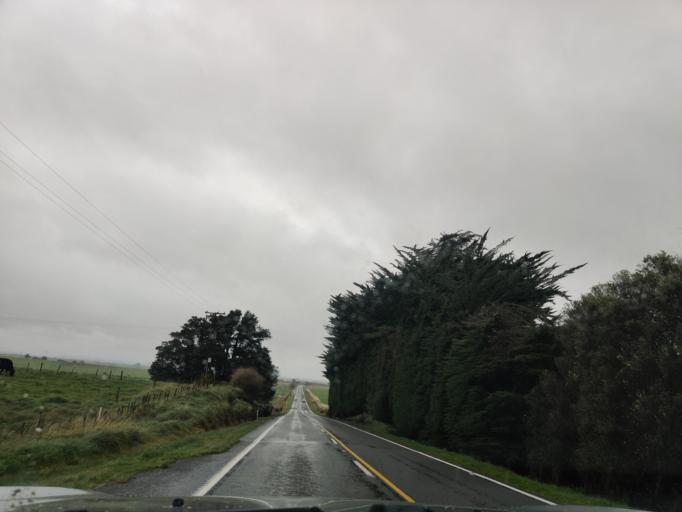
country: NZ
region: Hawke's Bay
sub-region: Hastings District
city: Hastings
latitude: -40.0366
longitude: 176.2556
